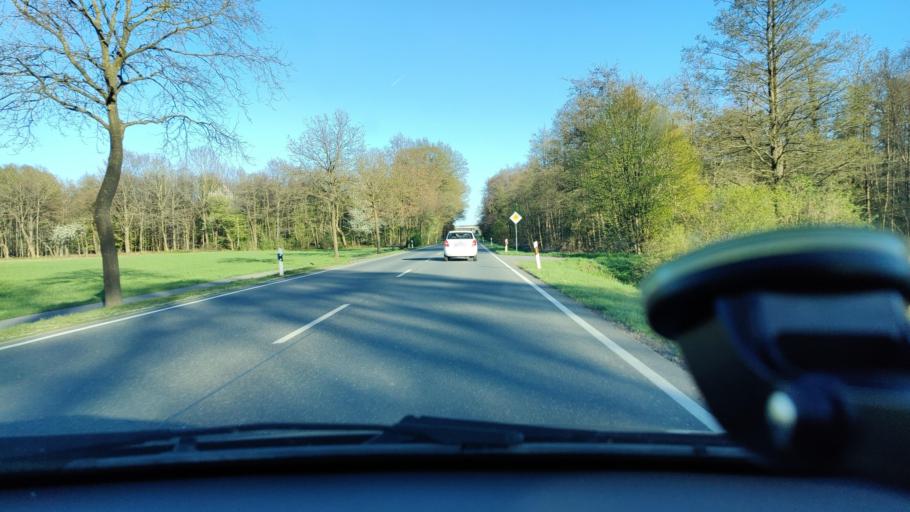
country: DE
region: North Rhine-Westphalia
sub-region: Regierungsbezirk Munster
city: Ahaus
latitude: 52.0532
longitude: 7.0550
